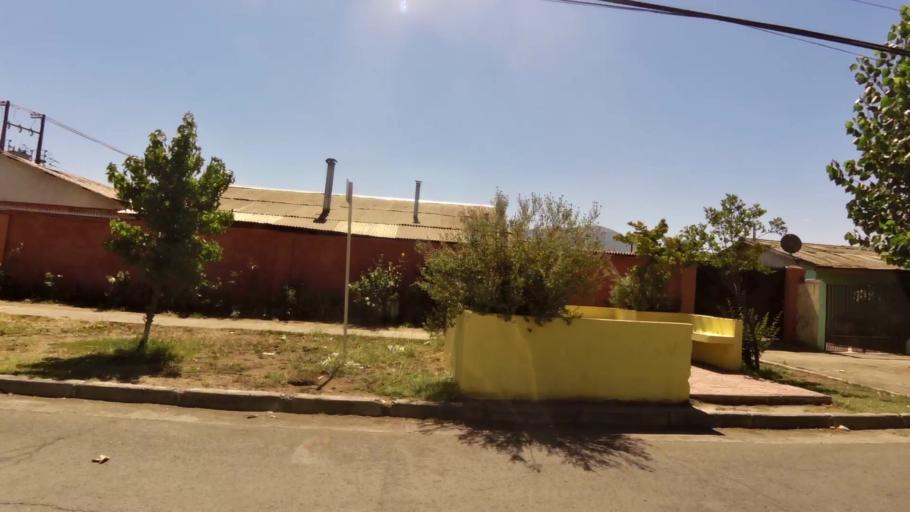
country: CL
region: O'Higgins
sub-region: Provincia de Colchagua
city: Chimbarongo
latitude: -34.5763
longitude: -70.9895
